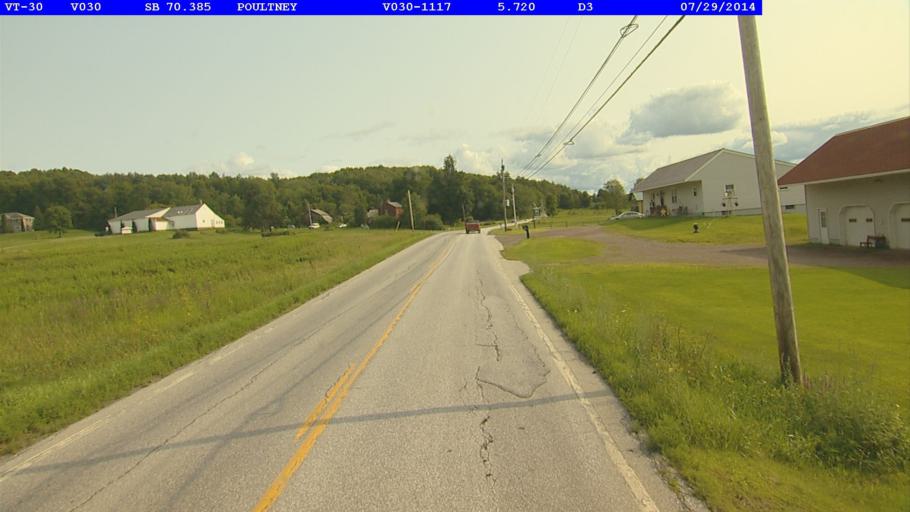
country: US
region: Vermont
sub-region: Rutland County
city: Poultney
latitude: 43.5332
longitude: -73.2288
